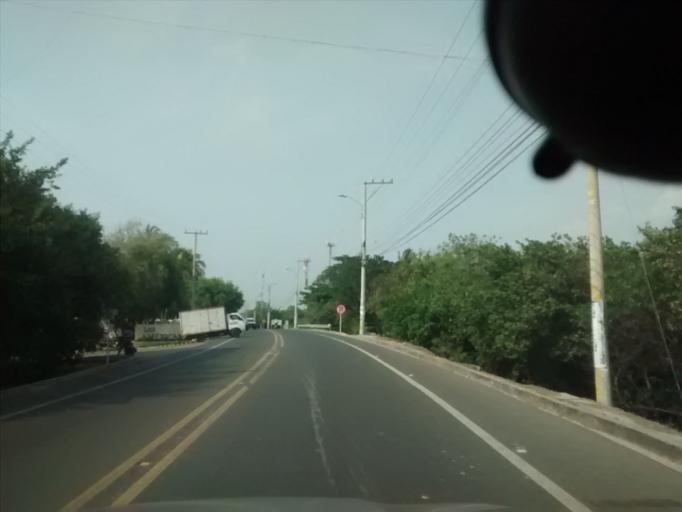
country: CO
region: Bolivar
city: Cartagena
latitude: 10.4590
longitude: -75.5068
